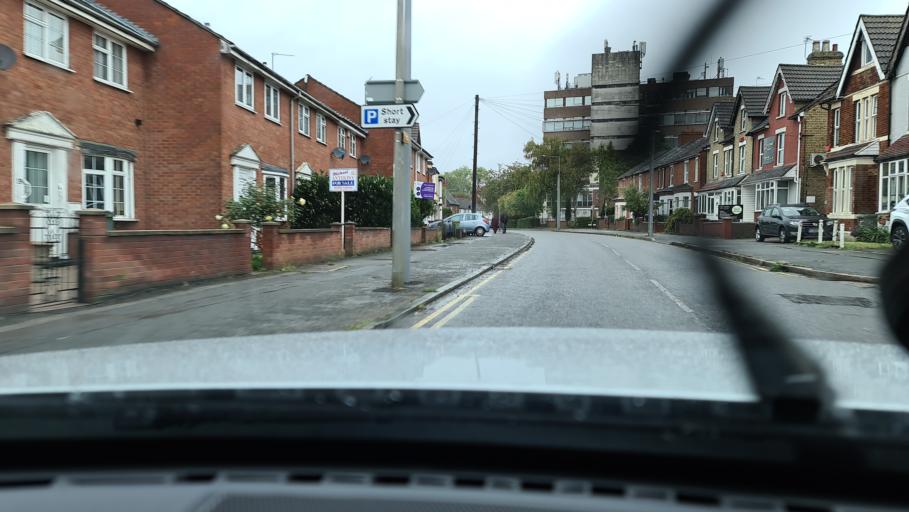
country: GB
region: England
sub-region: Milton Keynes
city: Water Eaton
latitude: 51.9978
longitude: -0.7197
